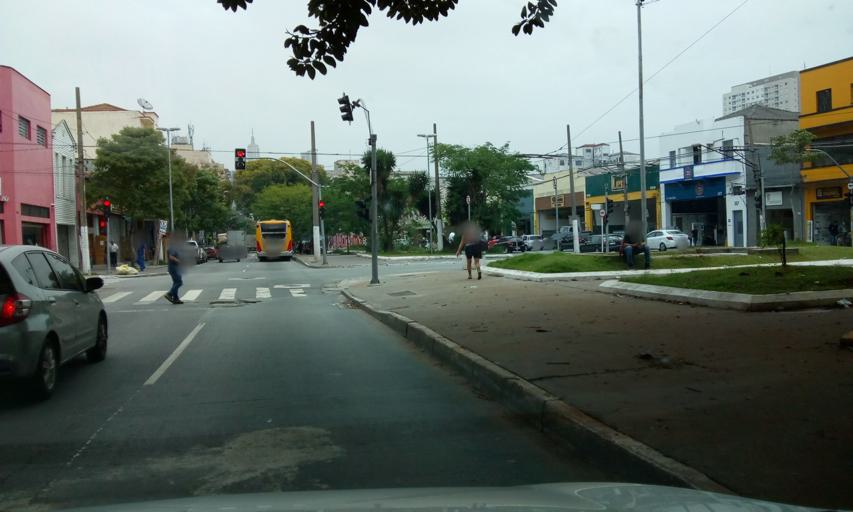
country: BR
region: Sao Paulo
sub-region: Sao Paulo
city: Sao Paulo
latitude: -23.5443
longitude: -46.6221
